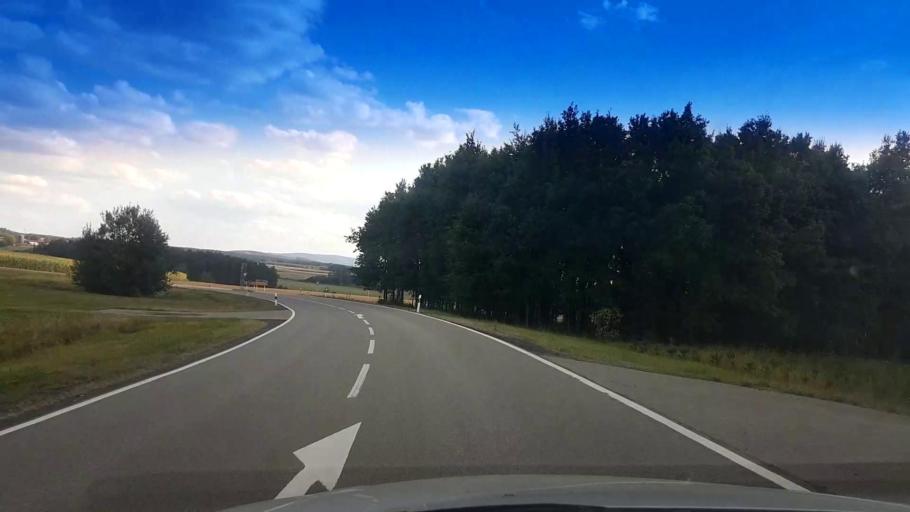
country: DE
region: Bavaria
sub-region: Upper Palatinate
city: Tirschenreuth
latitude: 49.8882
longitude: 12.3678
